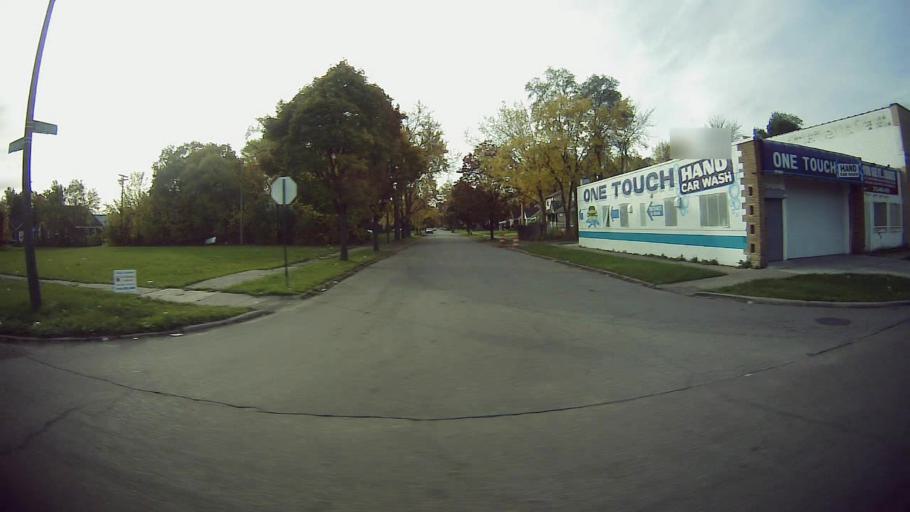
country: US
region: Michigan
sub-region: Oakland County
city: Oak Park
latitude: 42.4157
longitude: -83.2121
